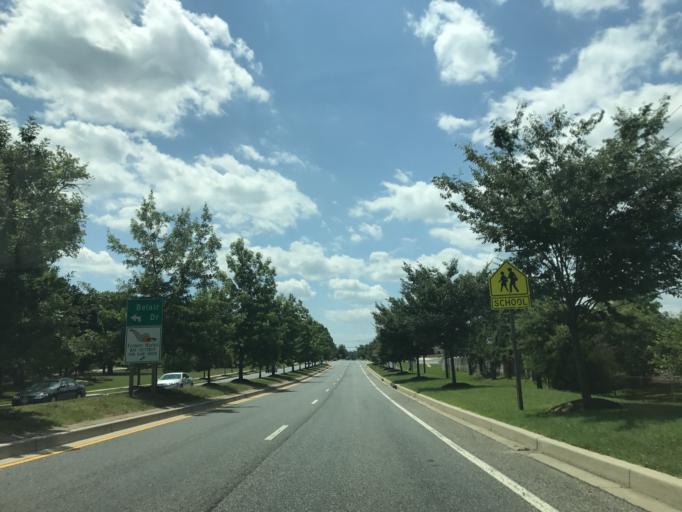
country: US
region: Maryland
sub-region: Prince George's County
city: Bowie
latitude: 38.9785
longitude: -76.7386
